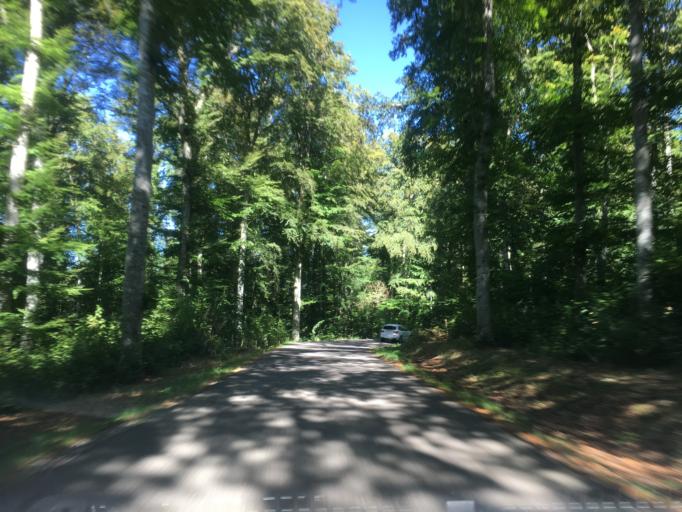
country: DE
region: Baden-Wuerttemberg
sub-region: Tuebingen Region
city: Pfullingen
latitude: 48.4147
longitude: 9.2173
